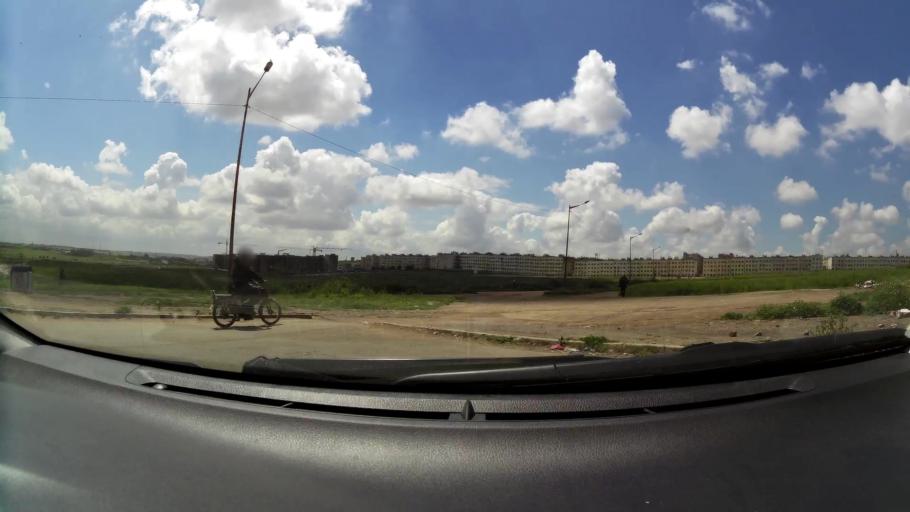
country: MA
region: Grand Casablanca
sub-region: Mediouna
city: Tit Mellil
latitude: 33.5425
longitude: -7.5475
